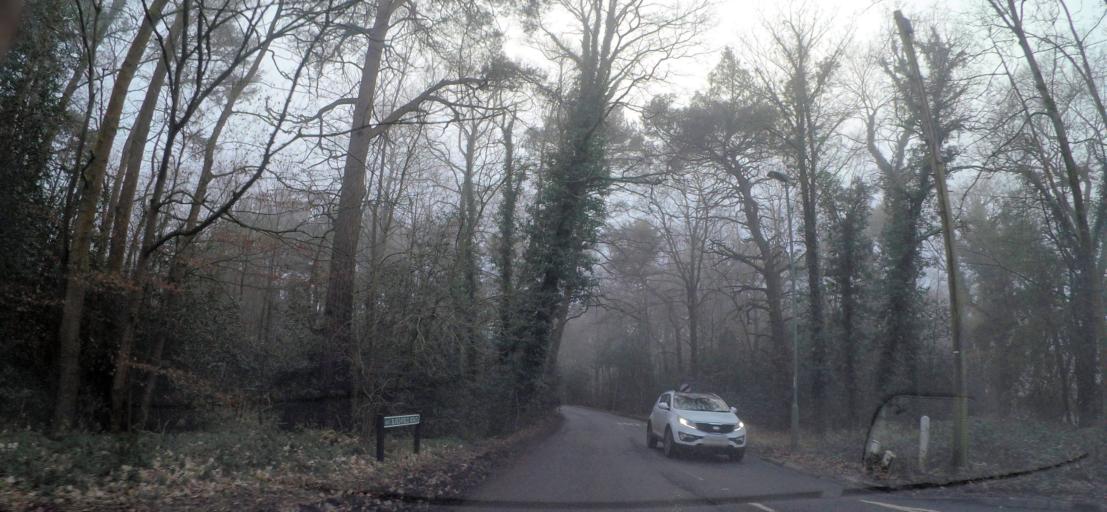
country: GB
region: England
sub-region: West Berkshire
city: Stratfield Mortimer
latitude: 51.3898
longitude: -1.0701
